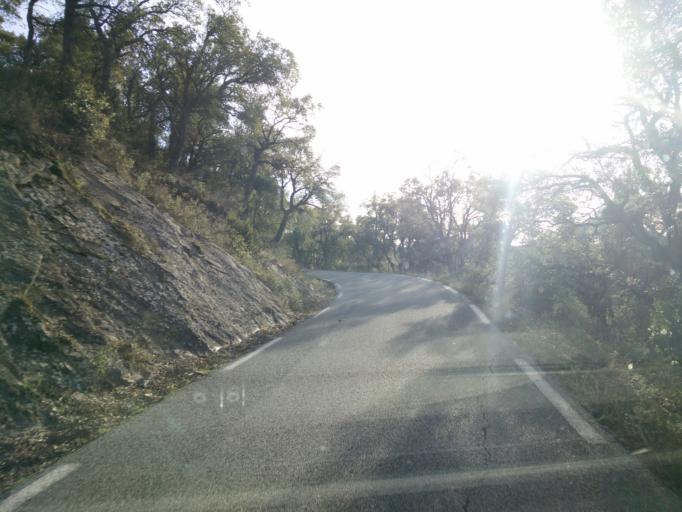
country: FR
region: Provence-Alpes-Cote d'Azur
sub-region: Departement du Var
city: Collobrieres
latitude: 43.2015
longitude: 6.3116
